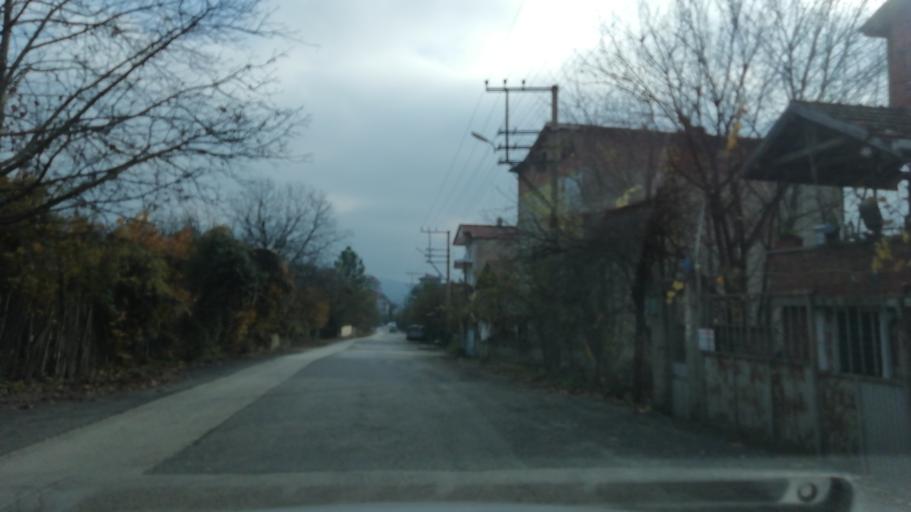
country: TR
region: Karabuk
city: Karabuk
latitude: 41.2246
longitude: 32.6242
